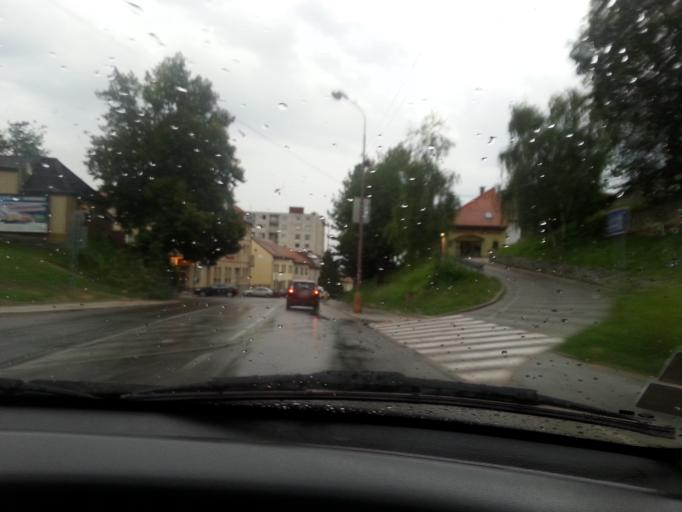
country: SK
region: Trenciansky
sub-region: Okres Nove Mesto nad Vahom
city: Nove Mesto nad Vahom
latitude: 48.7603
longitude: 17.8318
